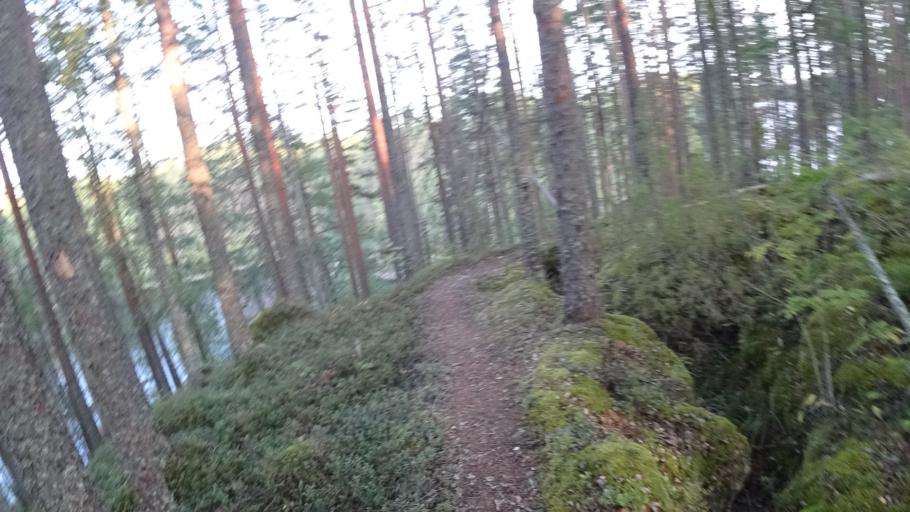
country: FI
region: North Karelia
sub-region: Joensuu
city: Ilomantsi
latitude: 62.5850
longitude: 31.1882
